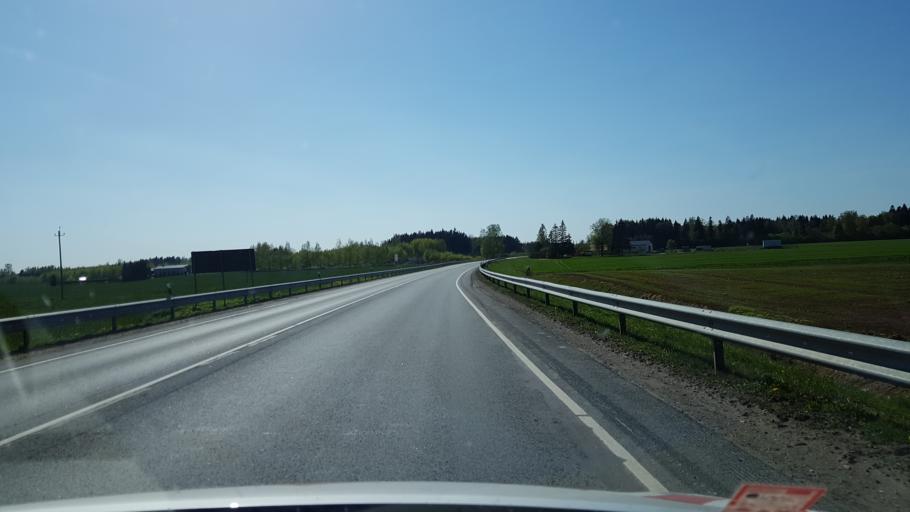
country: EE
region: Tartu
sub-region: Tartu linn
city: Tartu
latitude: 58.4100
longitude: 26.6261
